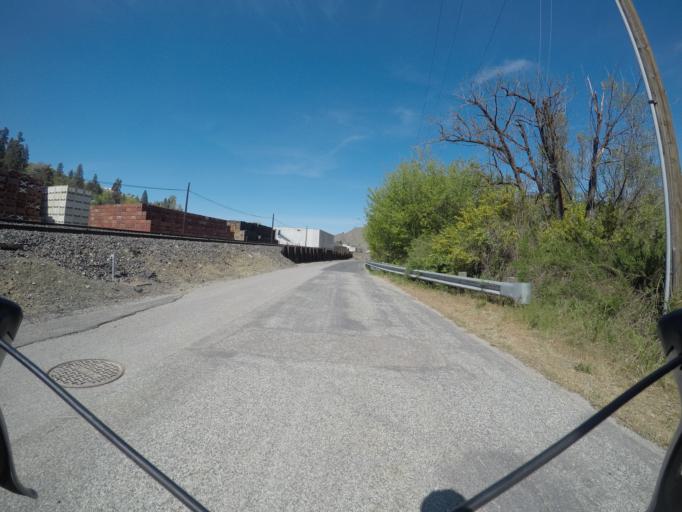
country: US
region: Washington
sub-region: Chelan County
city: Cashmere
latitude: 47.5154
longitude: -120.4568
